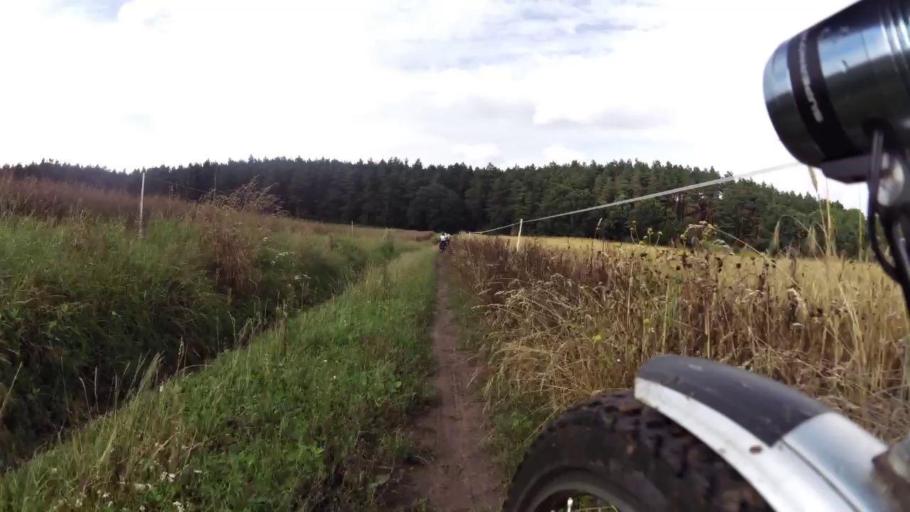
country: PL
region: West Pomeranian Voivodeship
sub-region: Powiat gryfinski
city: Banie
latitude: 53.1960
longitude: 14.5940
